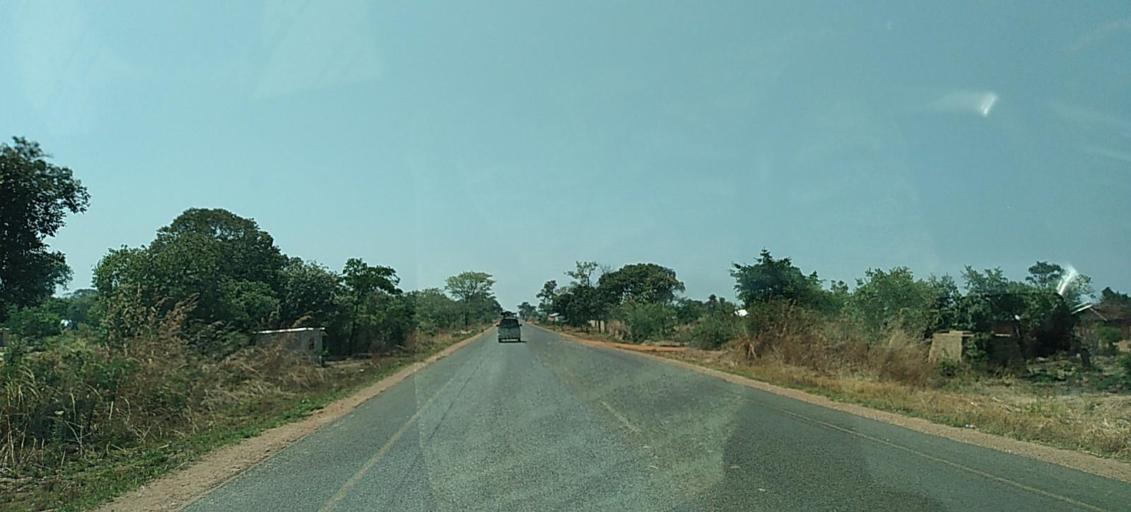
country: ZM
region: North-Western
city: Solwezi
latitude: -12.3035
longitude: 25.8350
